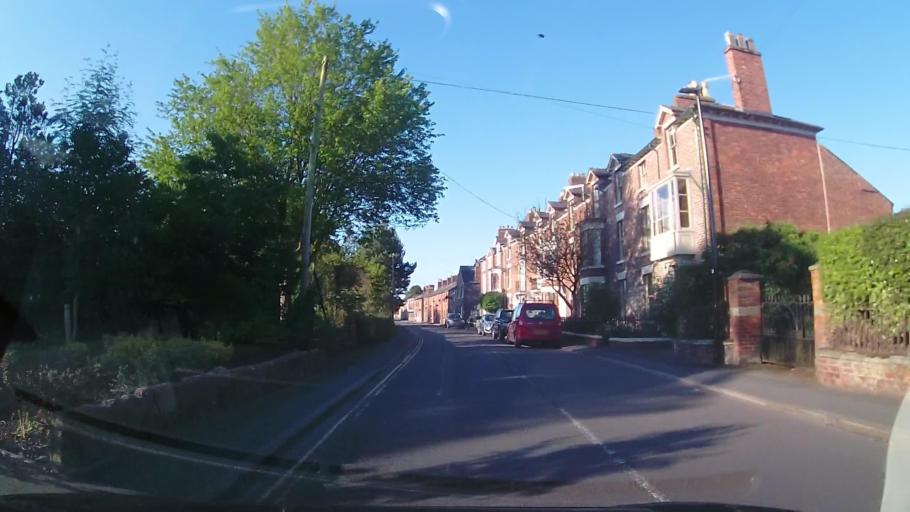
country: GB
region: England
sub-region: Shropshire
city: Wem
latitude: 52.8590
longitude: -2.7228
